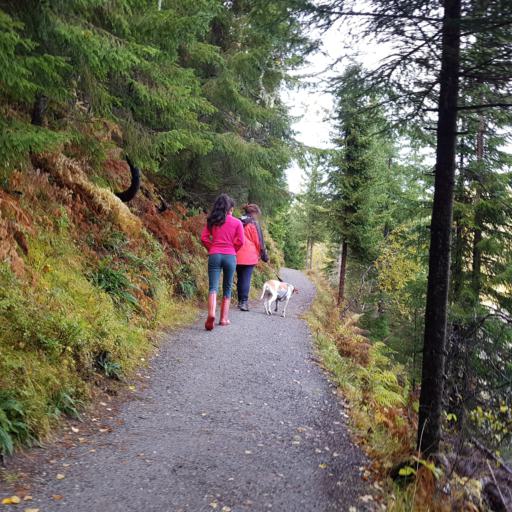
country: NO
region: Sor-Trondelag
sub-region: Trondheim
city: Trondheim
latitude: 63.4229
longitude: 10.2797
